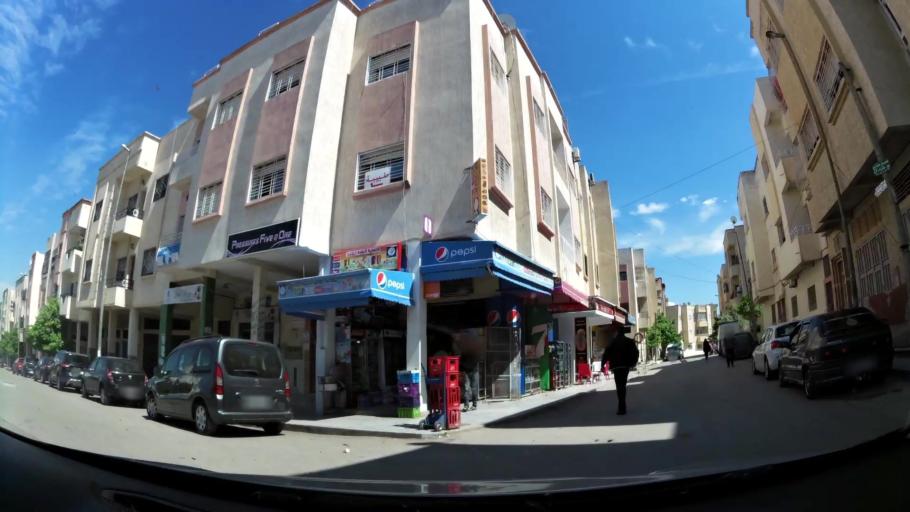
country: MA
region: Fes-Boulemane
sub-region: Fes
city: Fes
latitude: 34.0037
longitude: -4.9862
